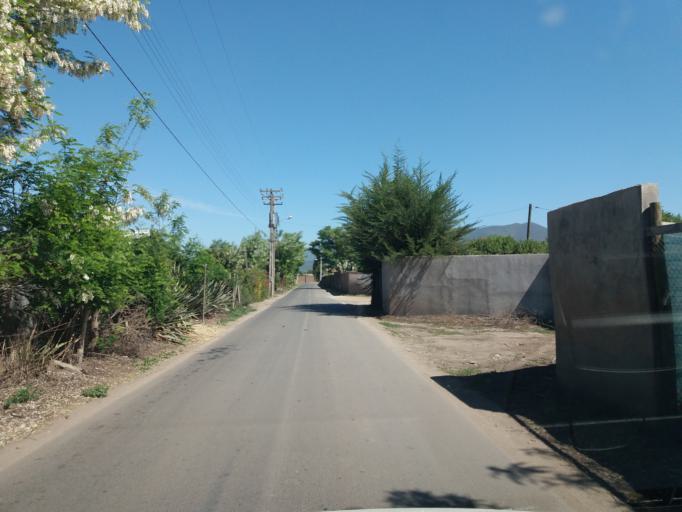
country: CL
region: Valparaiso
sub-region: Provincia de Quillota
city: Quillota
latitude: -32.8727
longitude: -71.2172
